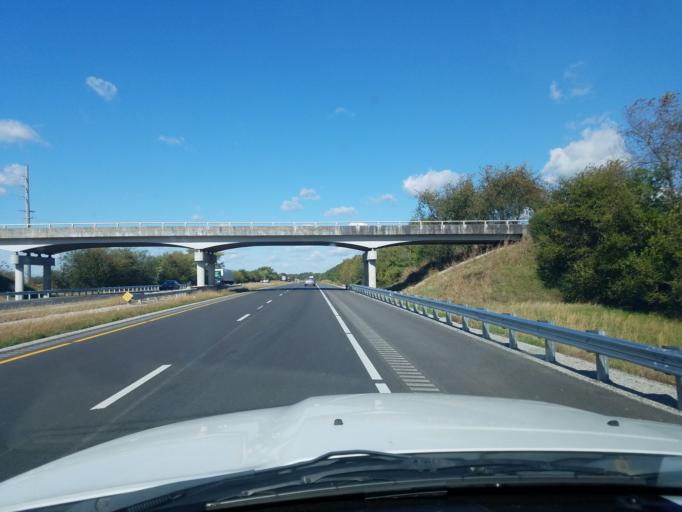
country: US
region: Kentucky
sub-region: Warren County
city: Plano
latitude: 36.9260
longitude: -86.4527
